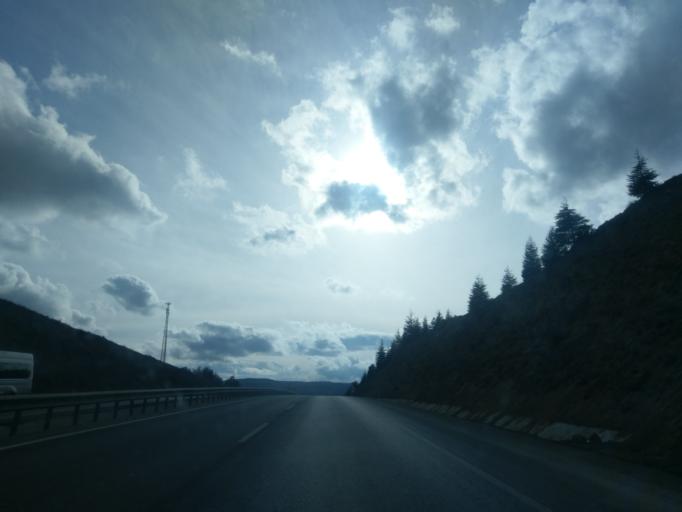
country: TR
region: Kuetahya
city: Sabuncu
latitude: 39.5807
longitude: 30.1225
